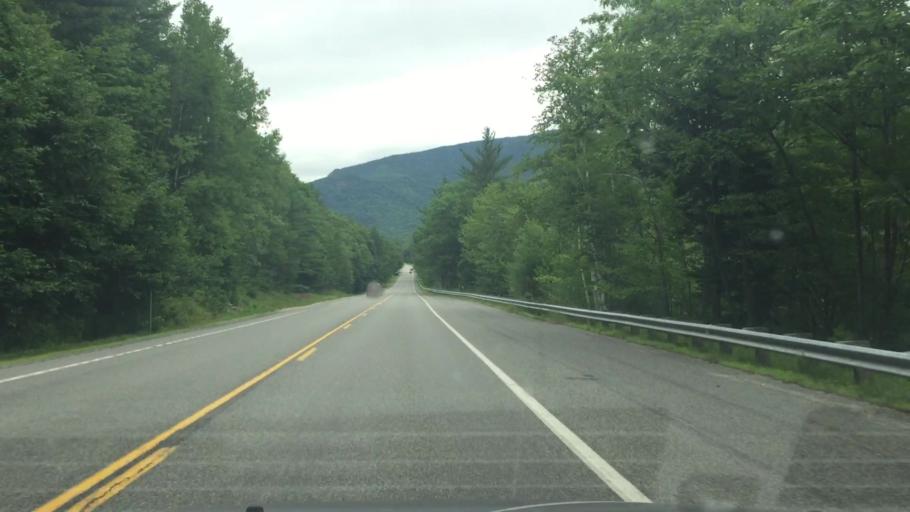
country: US
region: New Hampshire
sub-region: Carroll County
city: North Conway
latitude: 44.0981
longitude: -71.3547
